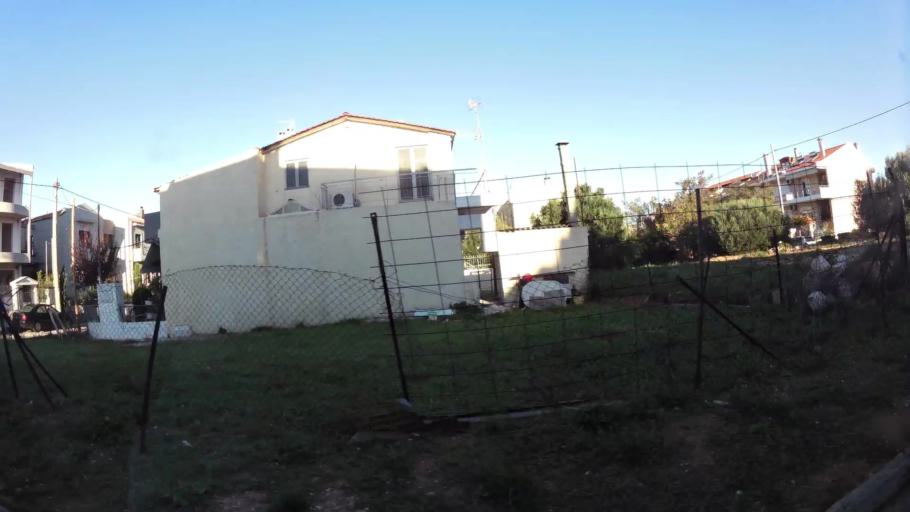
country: GR
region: Attica
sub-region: Nomarchia Anatolikis Attikis
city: Gerakas
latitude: 38.0314
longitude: 23.8493
